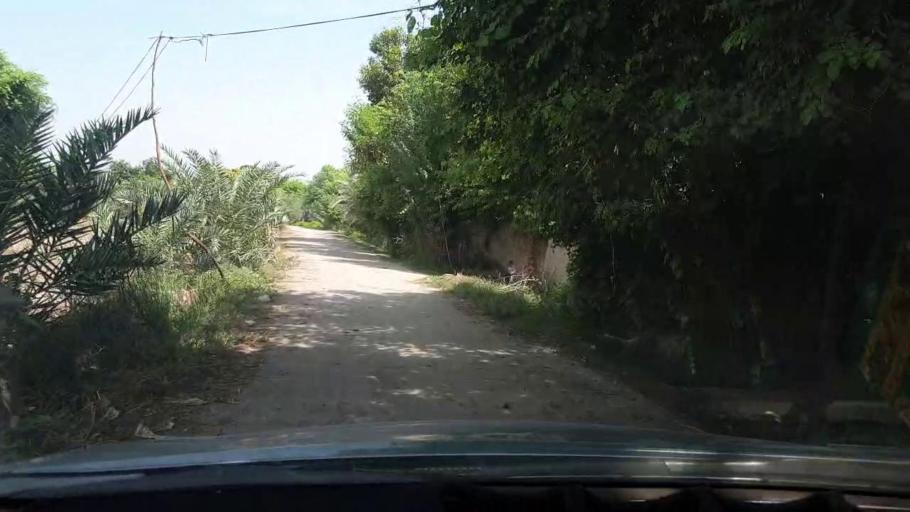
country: PK
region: Sindh
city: Khairpur
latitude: 27.4983
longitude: 68.7503
